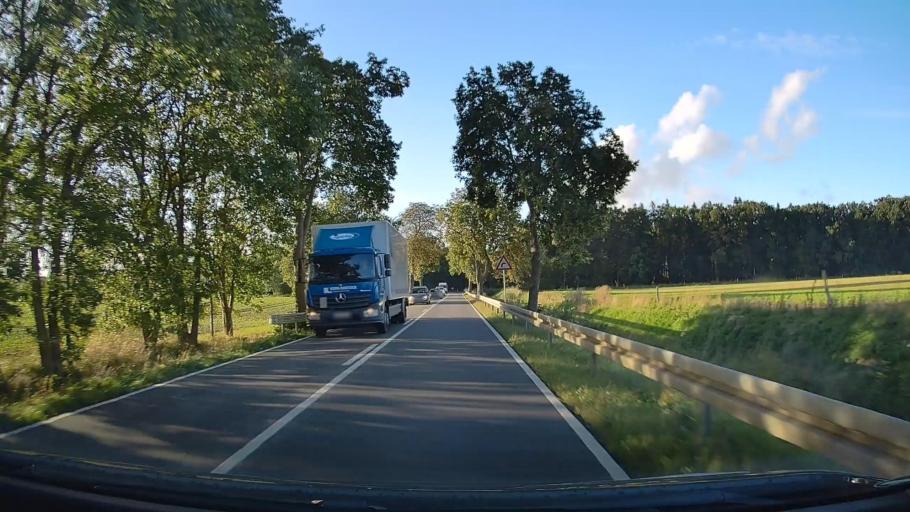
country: DE
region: Mecklenburg-Vorpommern
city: Steinhagen
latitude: 54.1983
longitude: 13.0129
